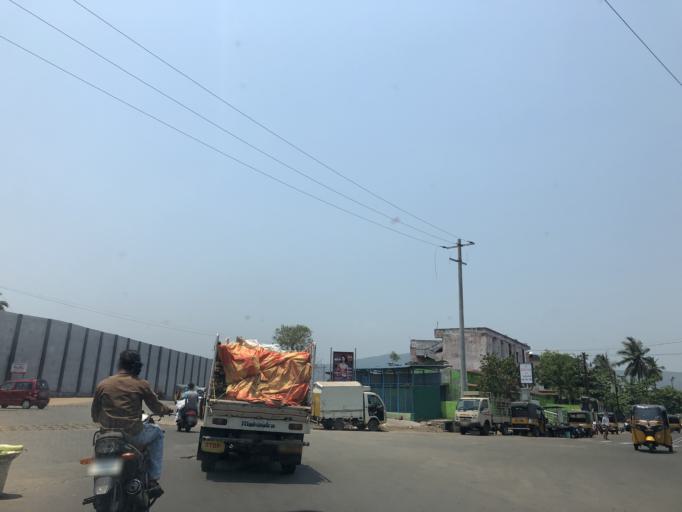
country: IN
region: Andhra Pradesh
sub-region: Vishakhapatnam
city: Yarada
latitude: 17.7109
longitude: 83.2941
